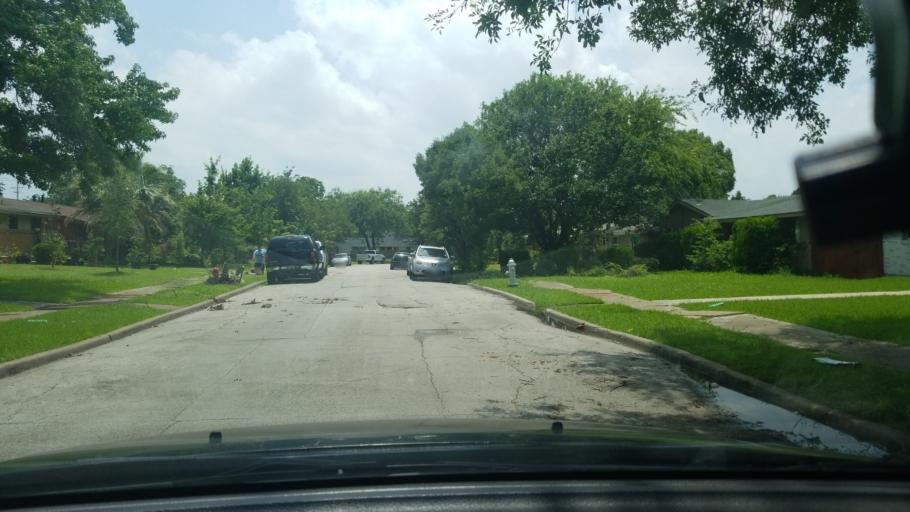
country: US
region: Texas
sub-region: Dallas County
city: Mesquite
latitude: 32.7948
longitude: -96.6364
